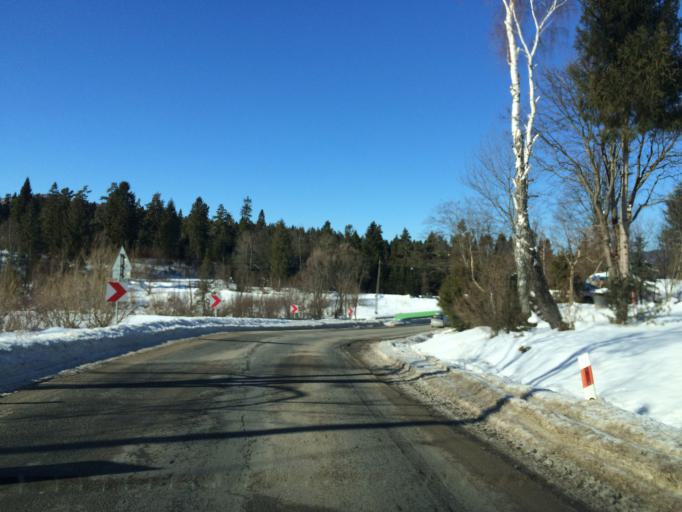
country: PL
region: Subcarpathian Voivodeship
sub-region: Powiat leski
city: Cisna
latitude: 49.1607
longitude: 22.4589
